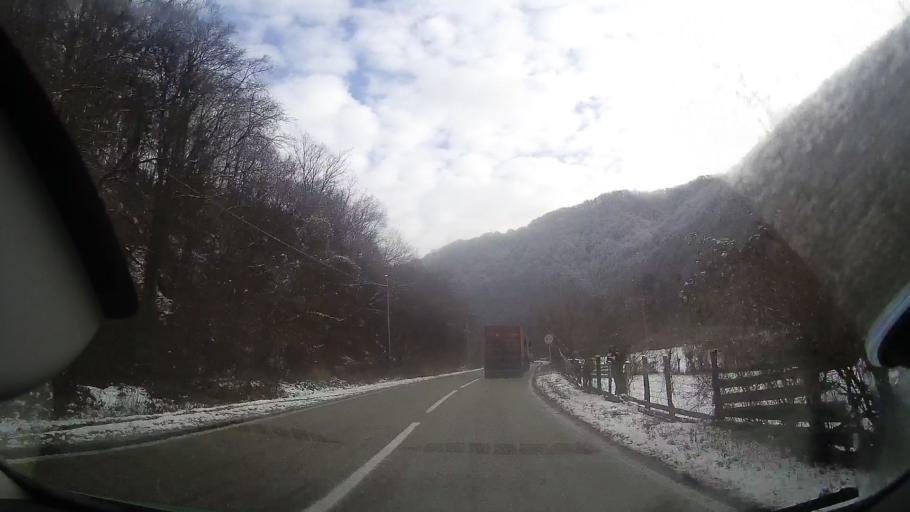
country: RO
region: Alba
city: Salciua de Sus
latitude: 46.4024
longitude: 23.3472
